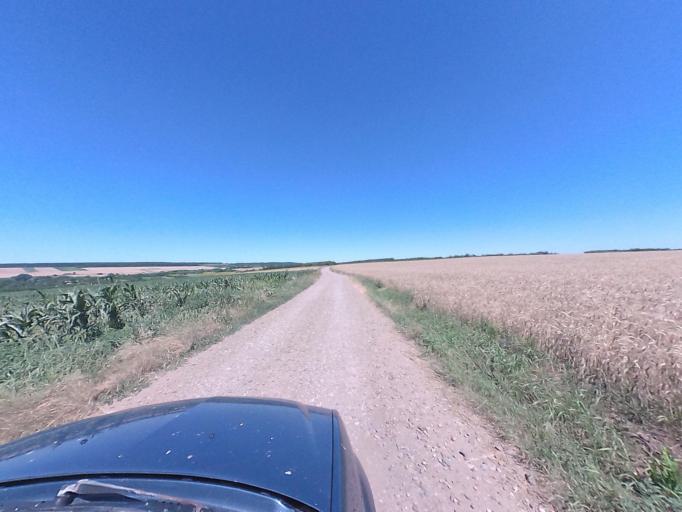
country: RO
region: Vaslui
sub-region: Comuna Costesti
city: Costesti
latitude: 46.4809
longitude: 27.7762
